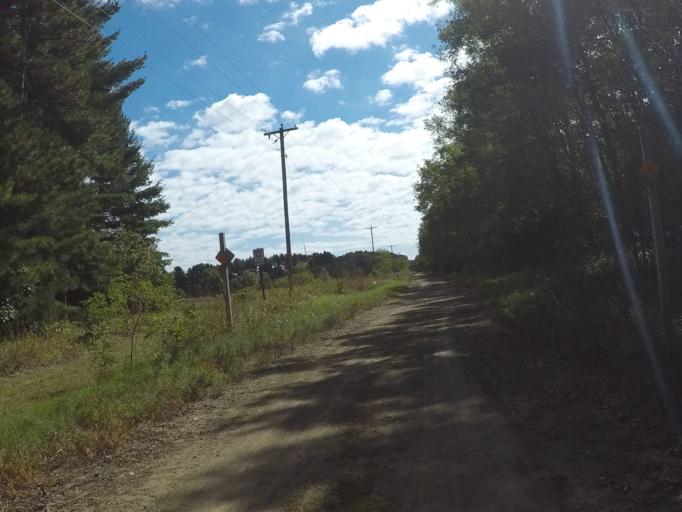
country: US
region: Wisconsin
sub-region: Sauk County
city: Spring Green
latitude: 43.1858
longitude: -90.2124
